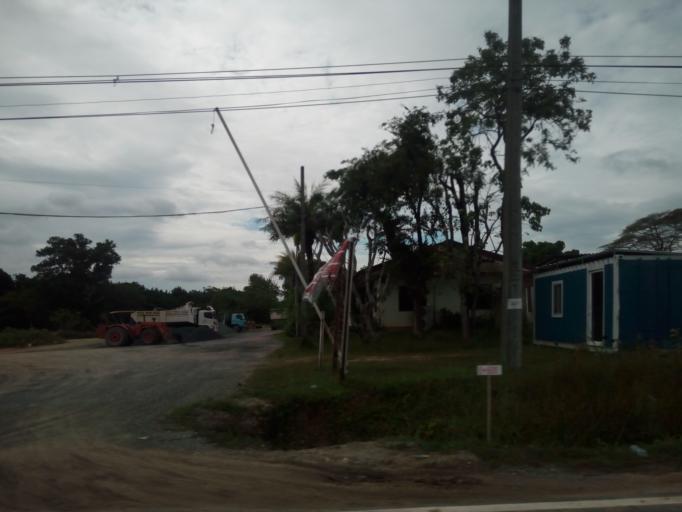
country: TH
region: Phuket
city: Ban Ko Kaeo
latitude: 7.9484
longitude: 98.3848
